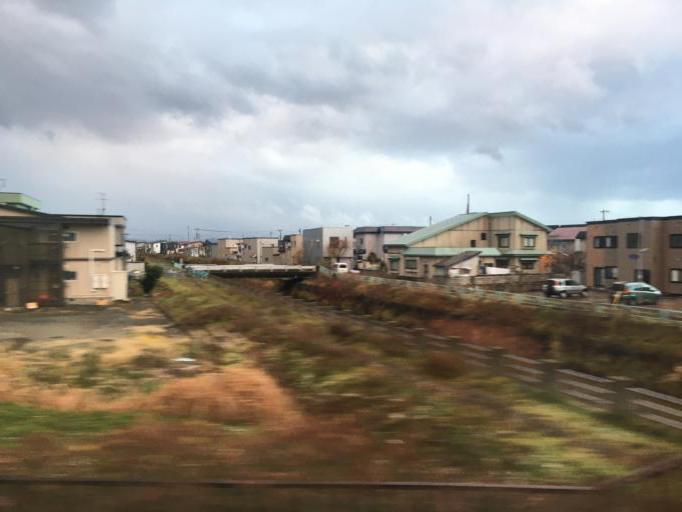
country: JP
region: Aomori
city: Aomori Shi
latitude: 40.8256
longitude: 140.7191
